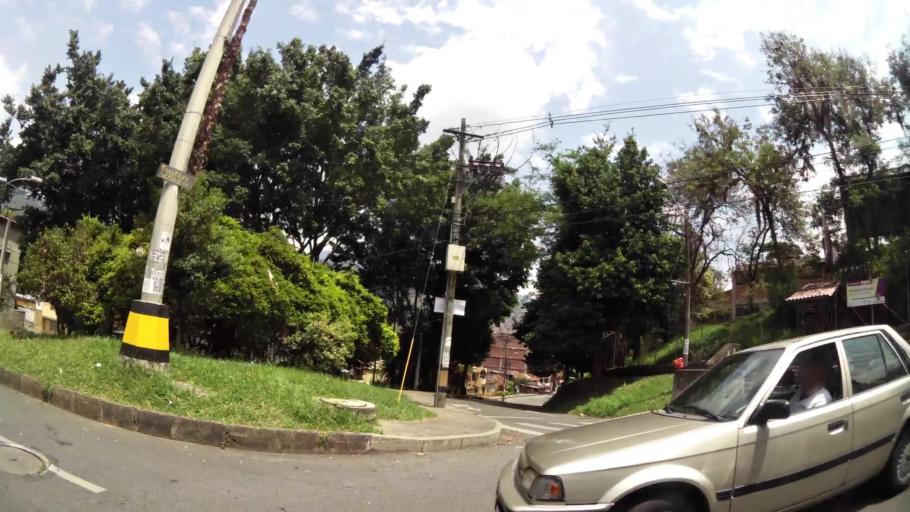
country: CO
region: Antioquia
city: Medellin
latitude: 6.2520
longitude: -75.6185
